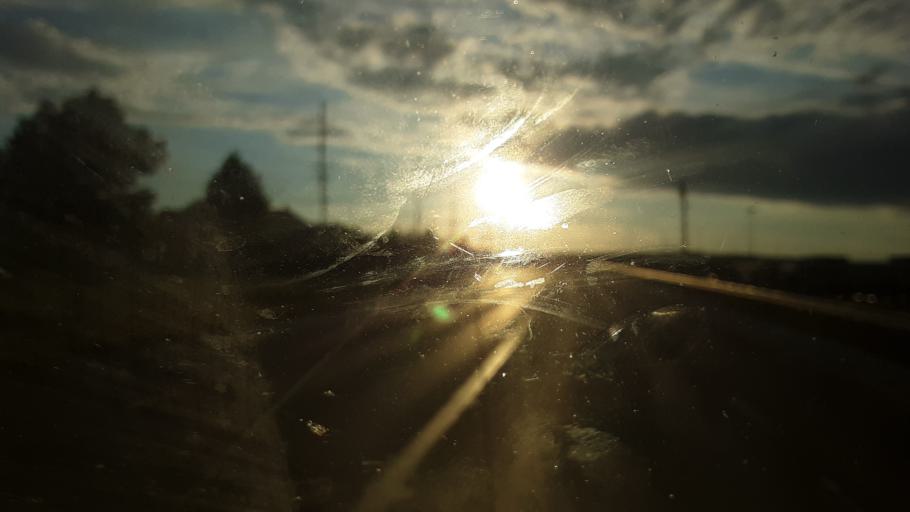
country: US
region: Maine
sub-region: Aroostook County
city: Presque Isle
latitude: 46.6970
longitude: -68.0028
